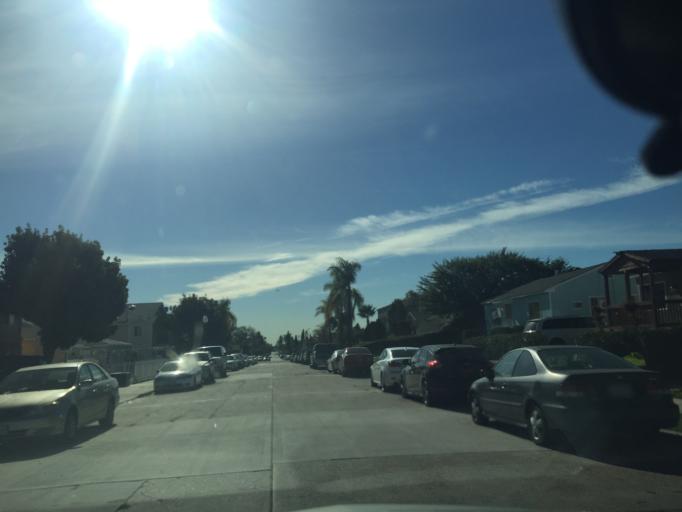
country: US
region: California
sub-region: San Diego County
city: Lemon Grove
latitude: 32.7576
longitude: -117.0912
